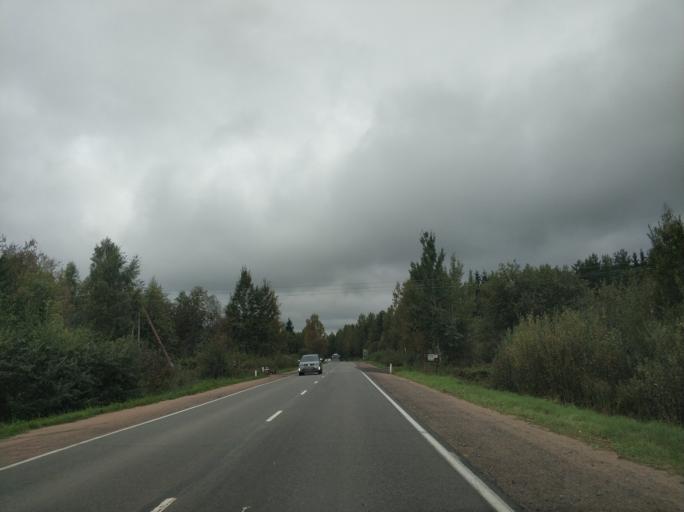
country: RU
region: Leningrad
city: Shcheglovo
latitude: 60.0959
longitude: 30.8467
